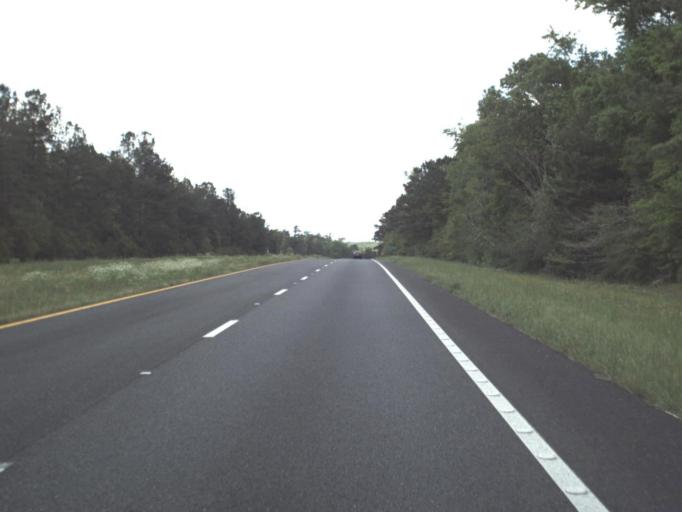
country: US
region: Florida
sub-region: Escambia County
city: Century
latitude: 30.8604
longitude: -87.3232
